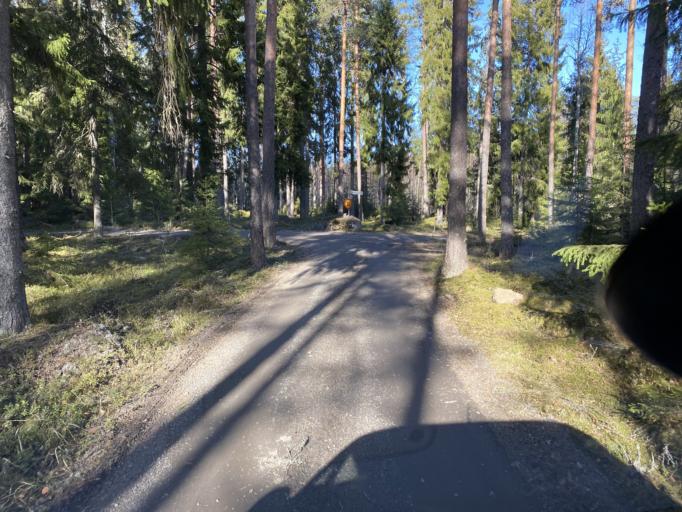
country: FI
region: Satakunta
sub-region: Rauma
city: Lappi
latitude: 61.1514
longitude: 21.8752
